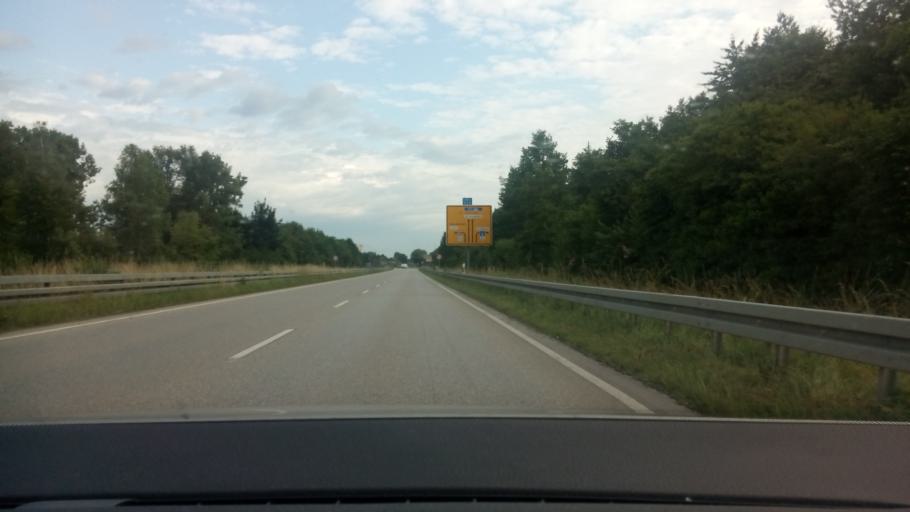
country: DE
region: Bavaria
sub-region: Upper Bavaria
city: Unterschleissheim
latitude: 48.2684
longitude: 11.5935
